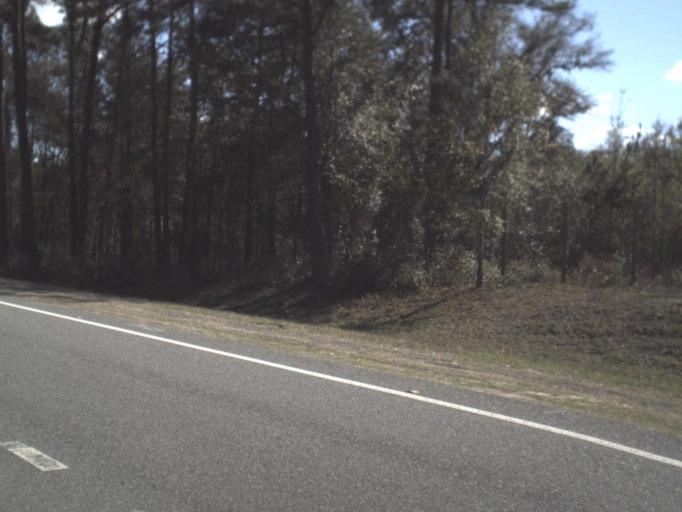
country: US
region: Florida
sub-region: Gadsden County
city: Midway
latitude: 30.4874
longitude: -84.4244
